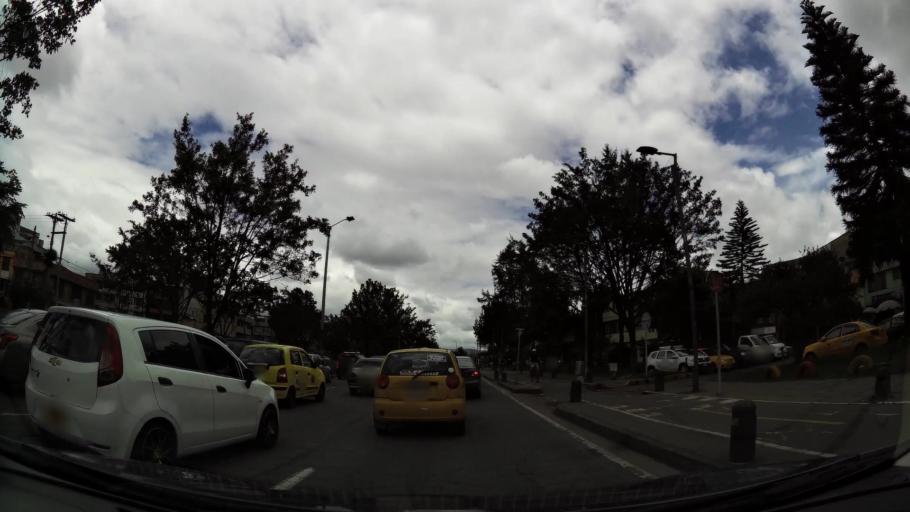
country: CO
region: Bogota D.C.
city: Bogota
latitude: 4.6866
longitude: -74.1119
